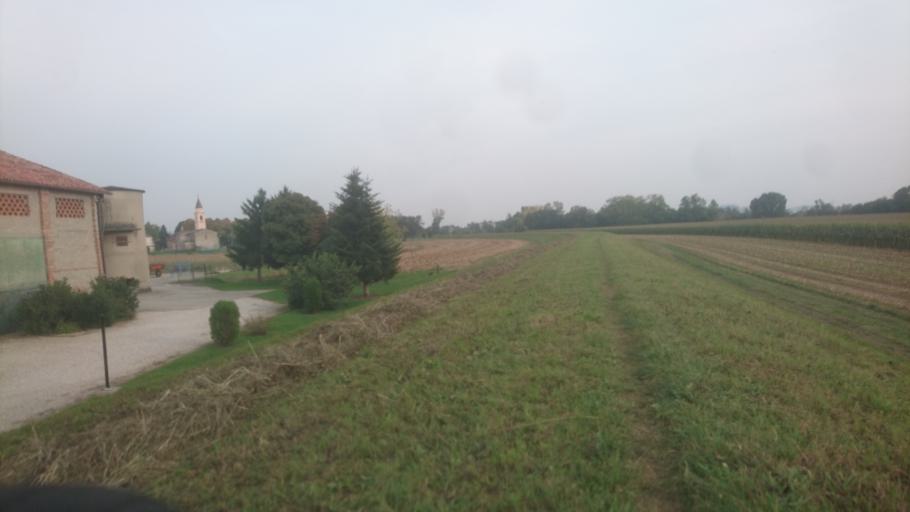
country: IT
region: Veneto
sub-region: Provincia di Padova
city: Cervarese Santa Croce
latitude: 45.4173
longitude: 11.7164
